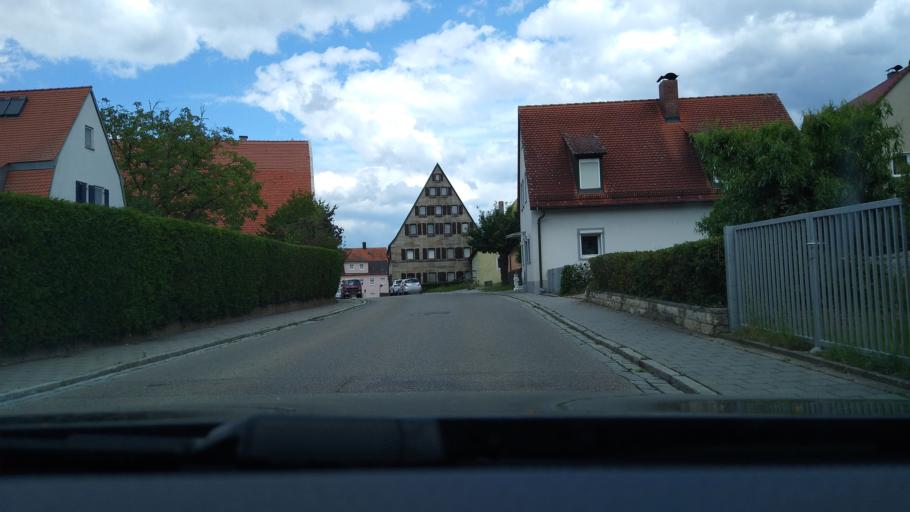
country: DE
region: Bavaria
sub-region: Regierungsbezirk Mittelfranken
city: Absberg
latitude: 49.1454
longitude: 10.8837
